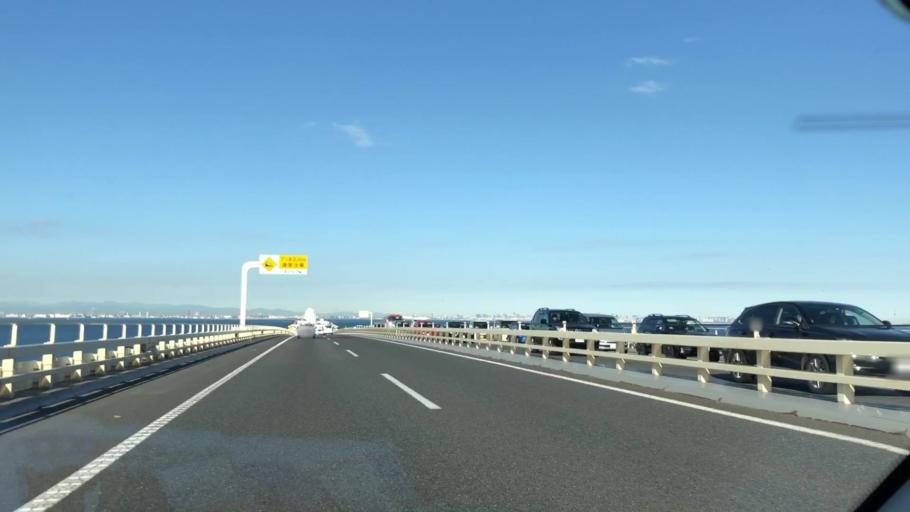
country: JP
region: Chiba
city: Kisarazu
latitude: 35.4563
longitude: 139.8861
